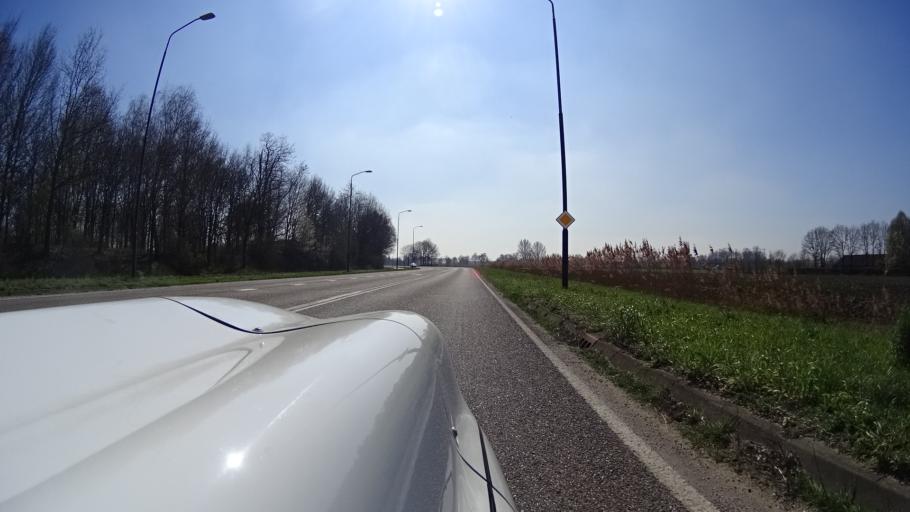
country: NL
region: North Brabant
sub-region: Gemeente Boekel
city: Boekel
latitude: 51.5530
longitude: 5.6730
